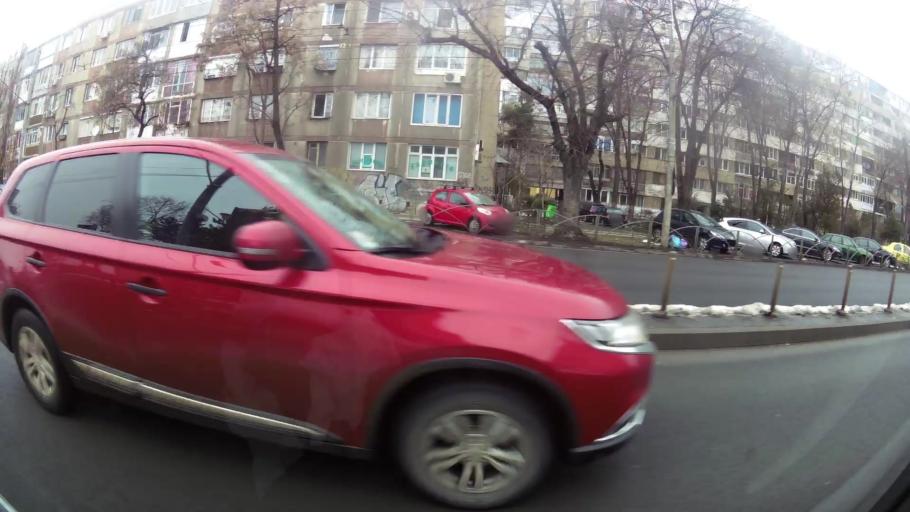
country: RO
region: Ilfov
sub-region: Comuna Chiajna
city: Rosu
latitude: 44.4182
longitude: 26.0405
